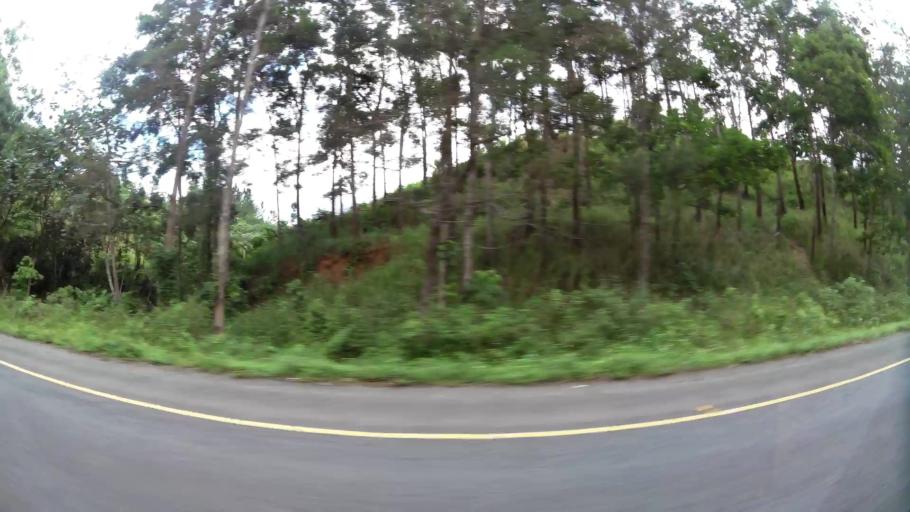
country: DO
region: Monsenor Nouel
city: Piedra Blanca
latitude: 18.8196
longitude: -70.2880
